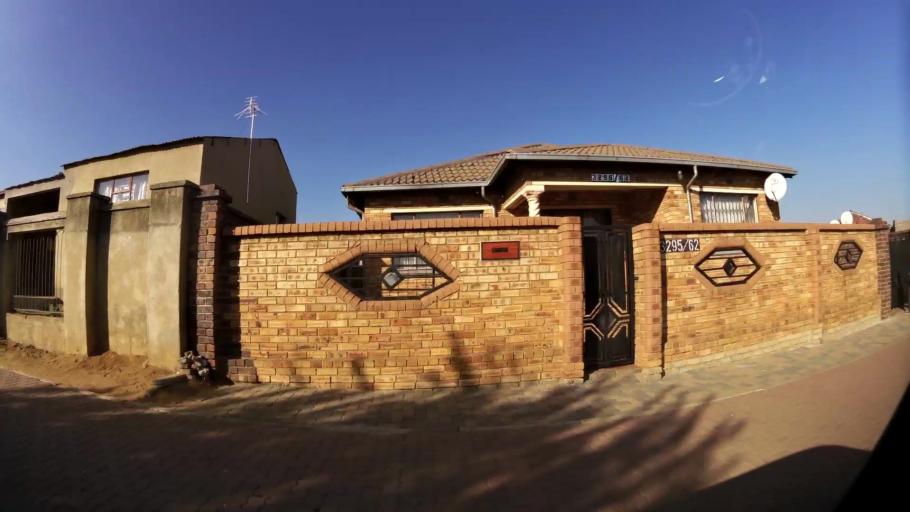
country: ZA
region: Gauteng
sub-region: City of Johannesburg Metropolitan Municipality
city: Soweto
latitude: -26.2296
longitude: 27.9306
